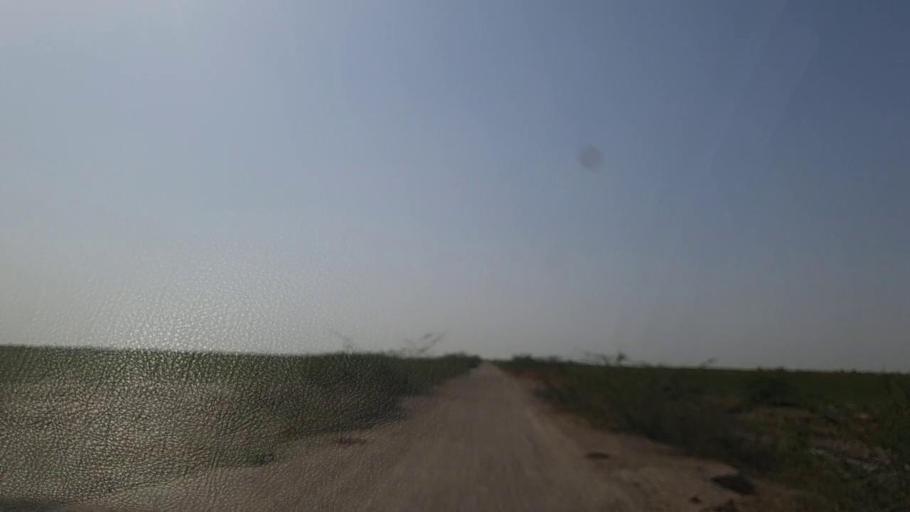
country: PK
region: Sindh
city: Naukot
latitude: 24.5925
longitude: 69.3035
